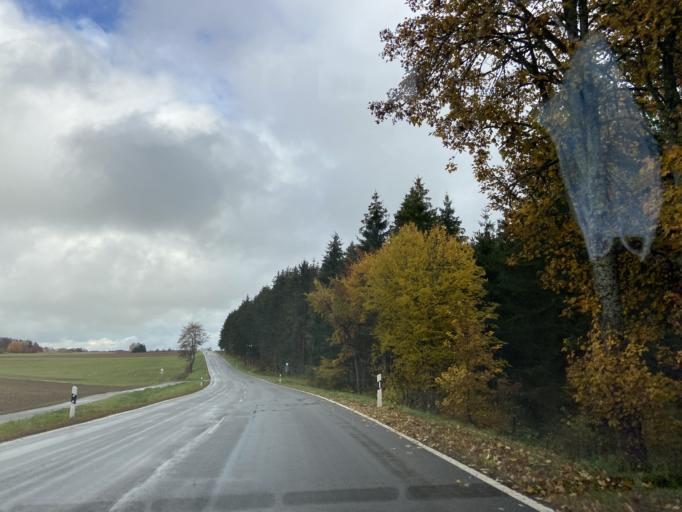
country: DE
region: Baden-Wuerttemberg
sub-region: Tuebingen Region
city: Schwenningen
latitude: 48.0938
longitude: 8.9815
